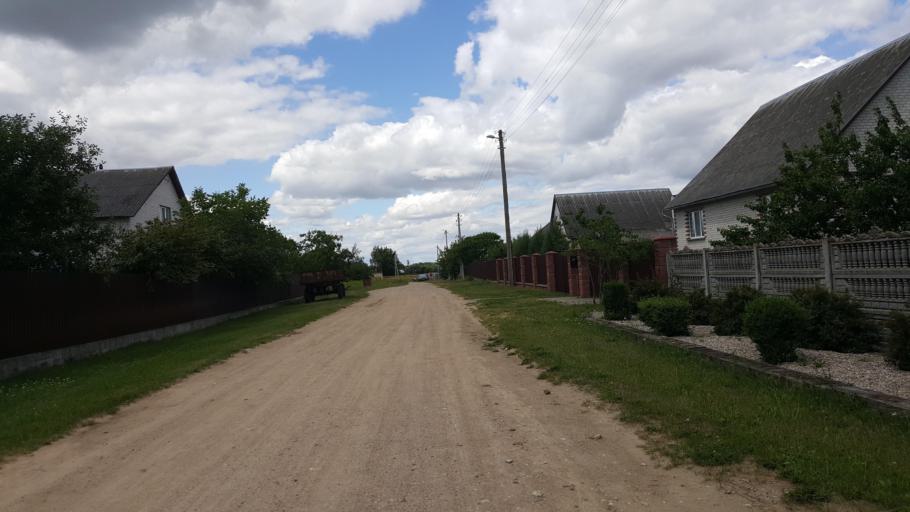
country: BY
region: Brest
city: Kamyanyets
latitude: 52.3203
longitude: 23.9276
